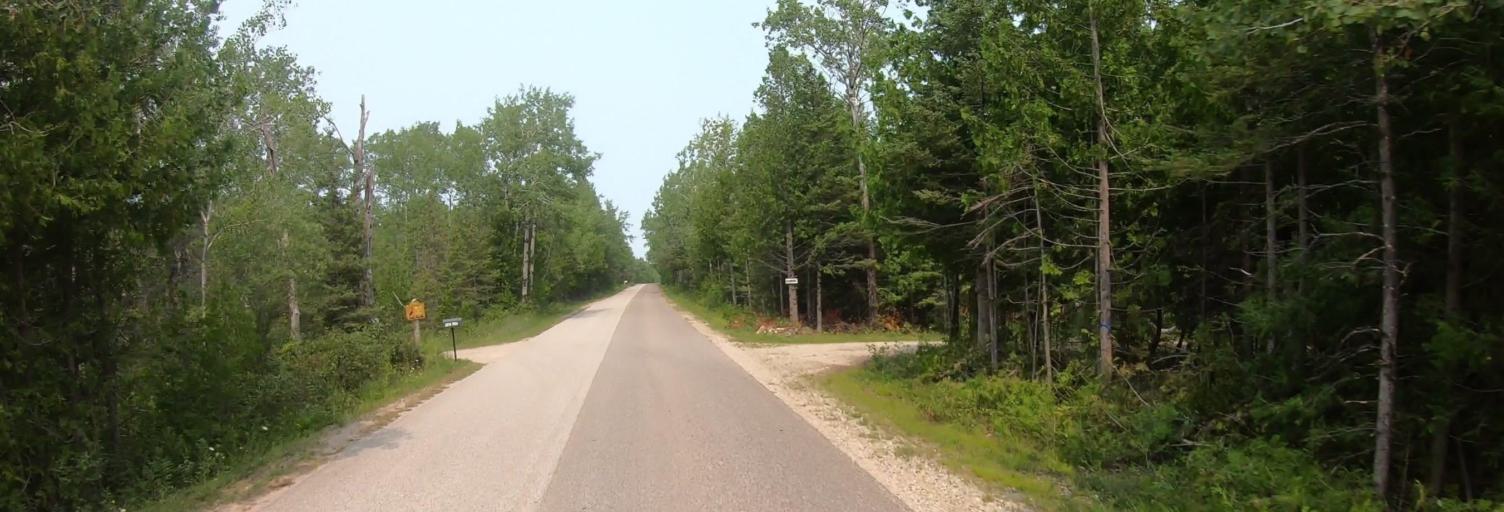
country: CA
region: Ontario
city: Thessalon
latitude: 46.0557
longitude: -83.6657
